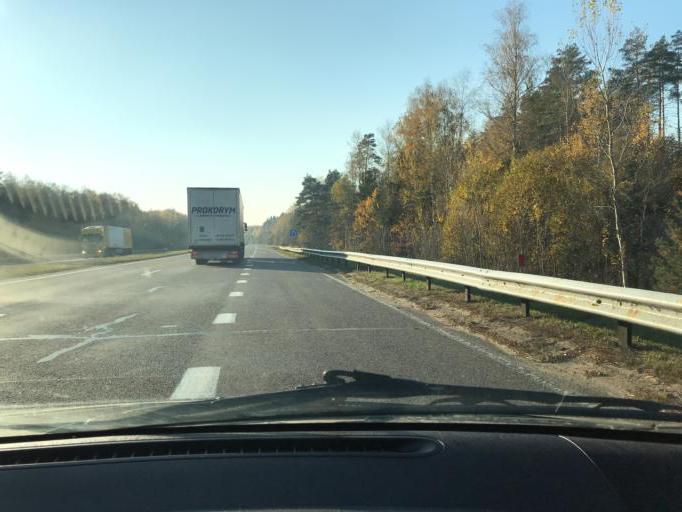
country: BY
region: Minsk
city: Loshnitsa
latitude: 54.2989
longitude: 28.9258
